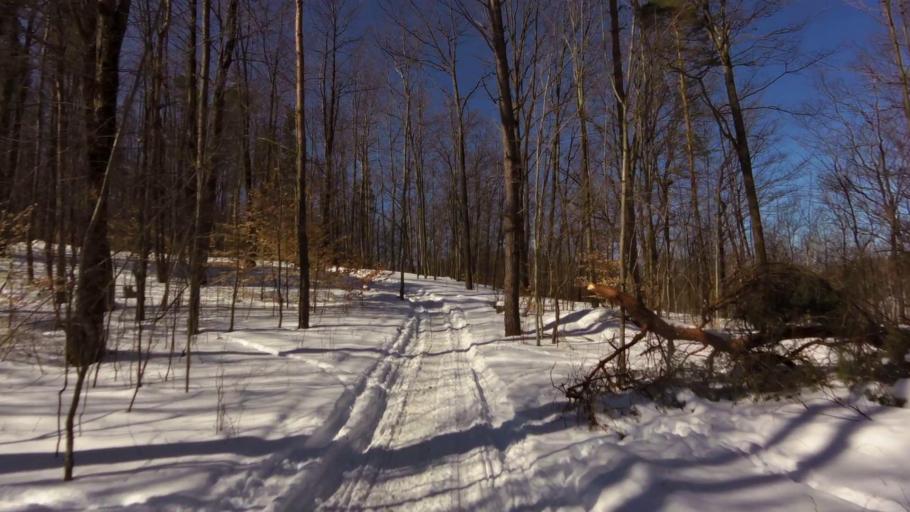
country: US
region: New York
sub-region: Allegany County
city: Cuba
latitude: 42.3191
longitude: -78.2758
